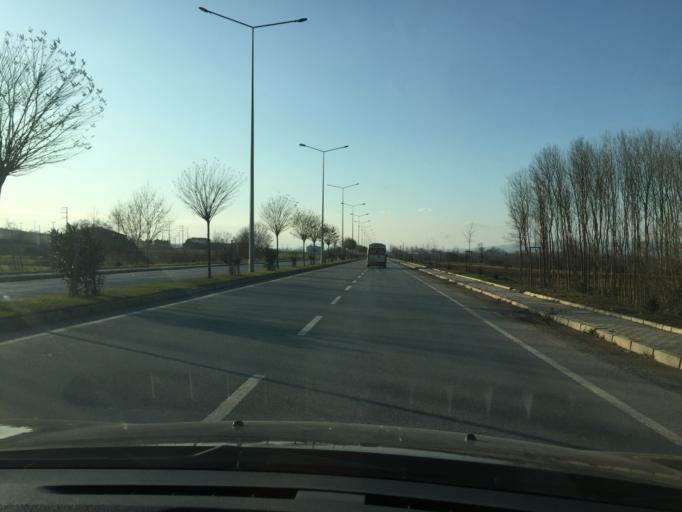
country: TR
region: Sakarya
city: Sogutlu
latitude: 40.9024
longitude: 30.5006
